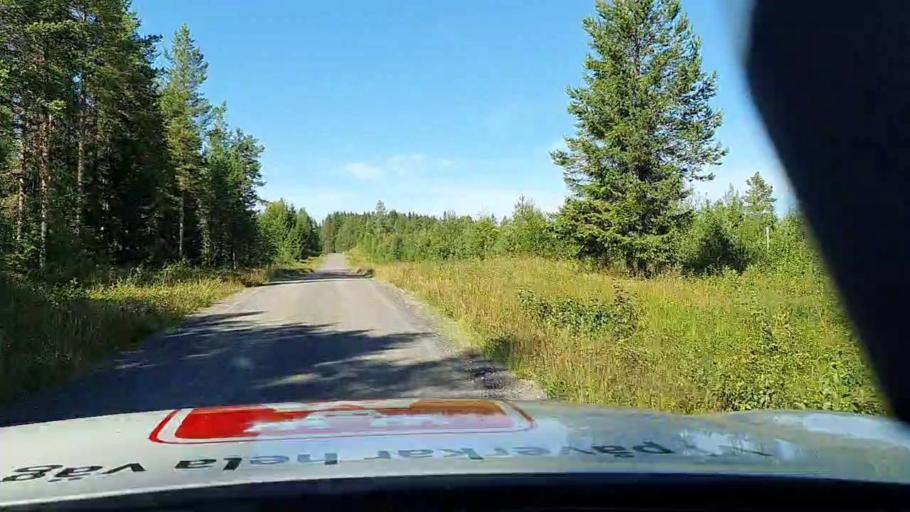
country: SE
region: Jaemtland
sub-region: OEstersunds Kommun
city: Lit
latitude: 63.7695
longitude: 14.6563
